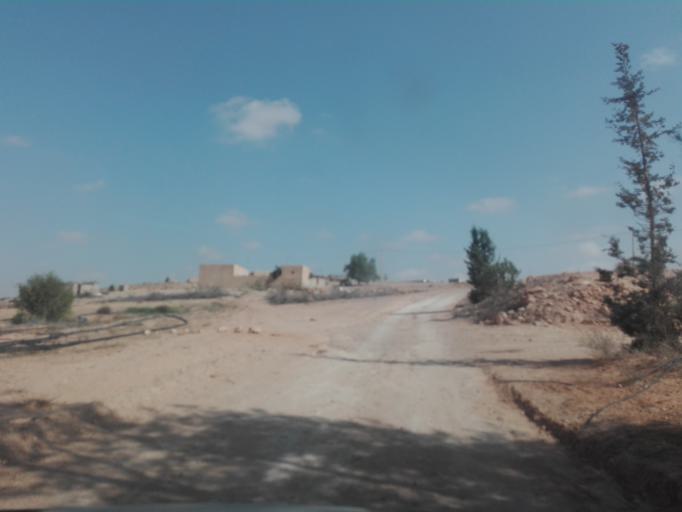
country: TN
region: Madanin
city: Medenine
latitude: 33.4386
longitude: 10.4317
